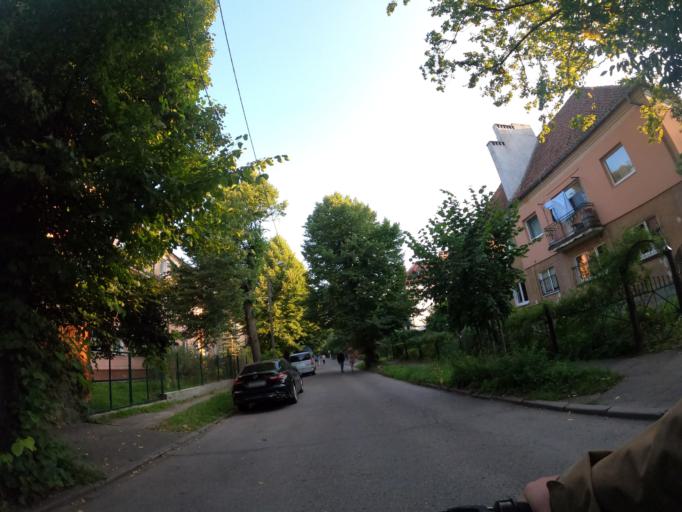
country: RU
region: Kaliningrad
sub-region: Gorod Kaliningrad
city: Kaliningrad
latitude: 54.7194
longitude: 20.4625
